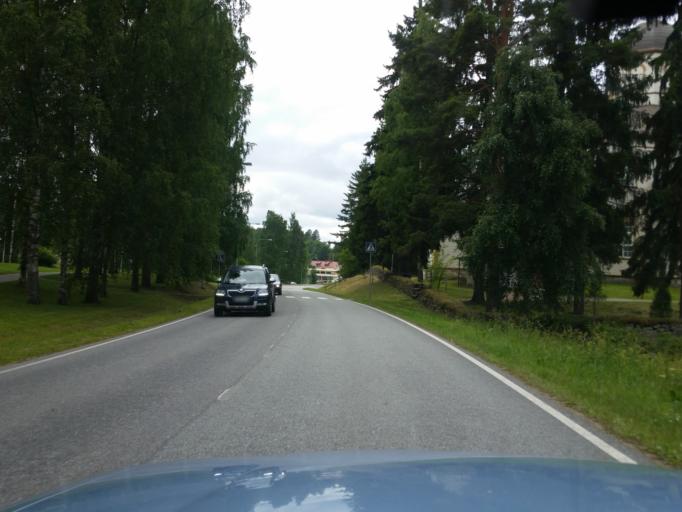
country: FI
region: Southern Savonia
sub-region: Savonlinna
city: Sulkava
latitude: 61.7901
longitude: 28.3750
